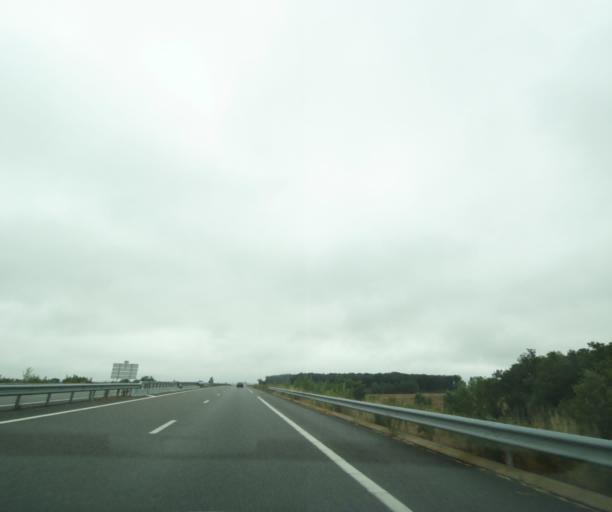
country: FR
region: Midi-Pyrenees
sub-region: Departement du Tarn
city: Le Garric
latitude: 44.0236
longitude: 2.1856
